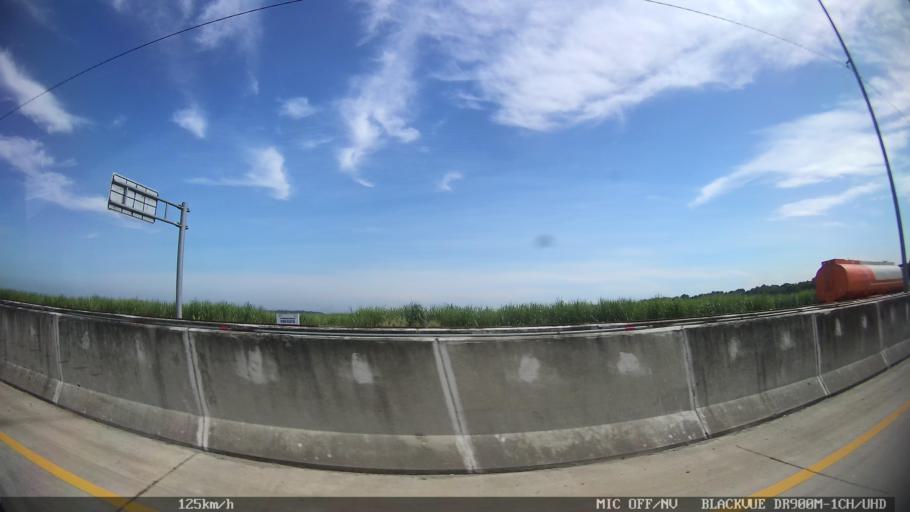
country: ID
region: North Sumatra
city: Sunggal
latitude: 3.6379
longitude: 98.6316
